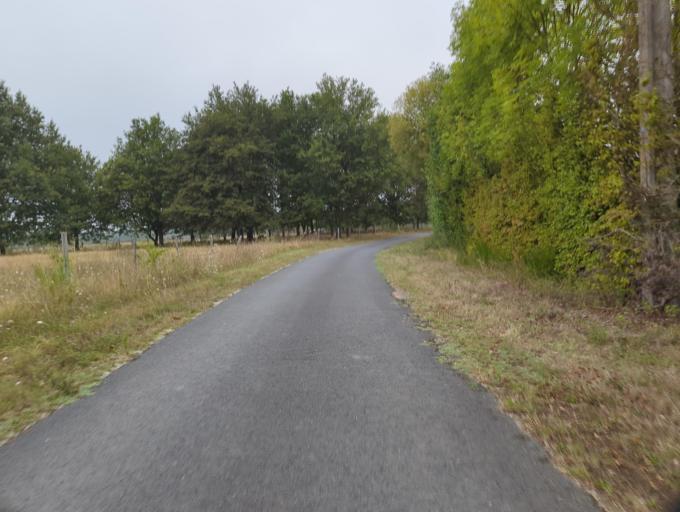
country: FR
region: Pays de la Loire
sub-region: Departement de Maine-et-Loire
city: Le Plessis-Grammoire
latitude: 47.4768
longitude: -0.4397
